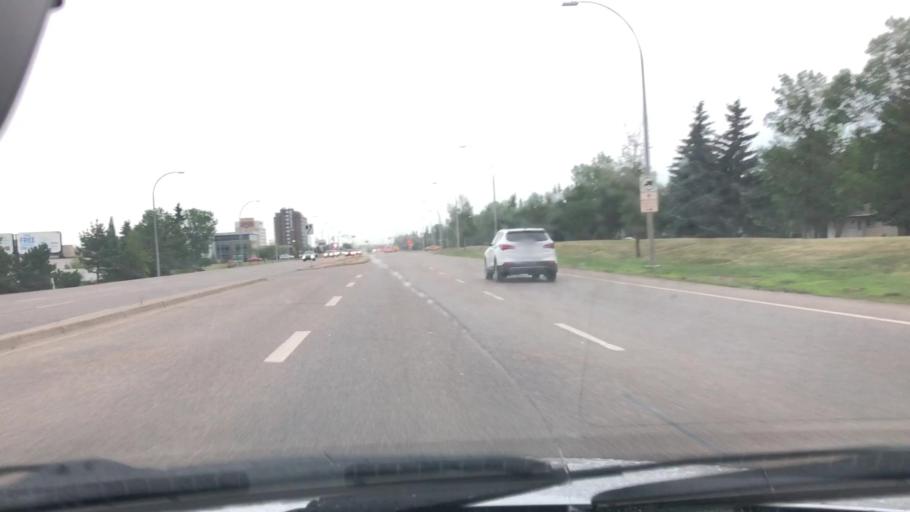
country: CA
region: Alberta
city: St. Albert
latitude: 53.5495
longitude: -113.6104
